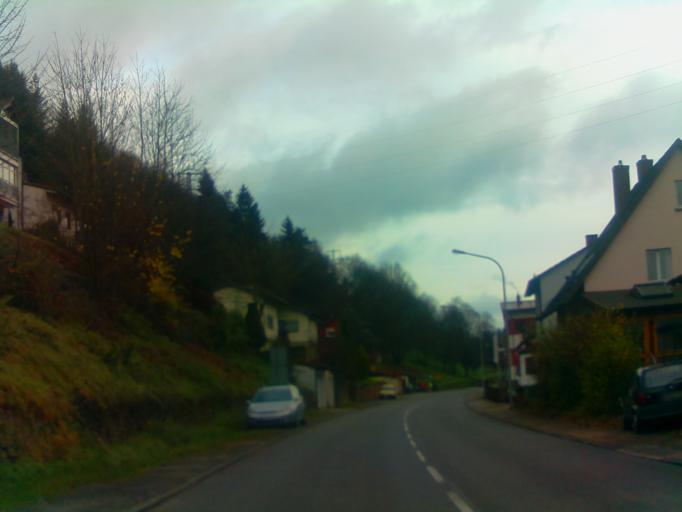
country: DE
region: Hesse
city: Hirschhorn
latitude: 49.4540
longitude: 8.8947
